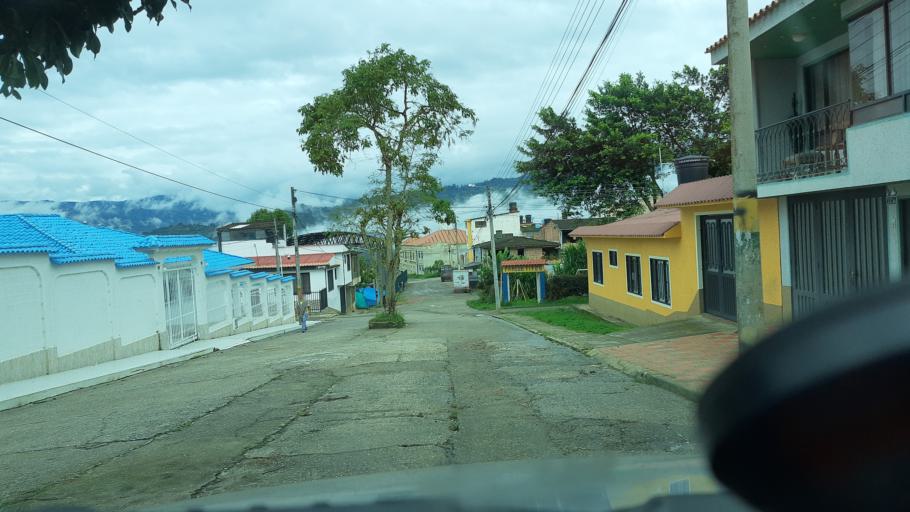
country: CO
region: Boyaca
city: Garagoa
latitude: 5.0848
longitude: -73.3661
